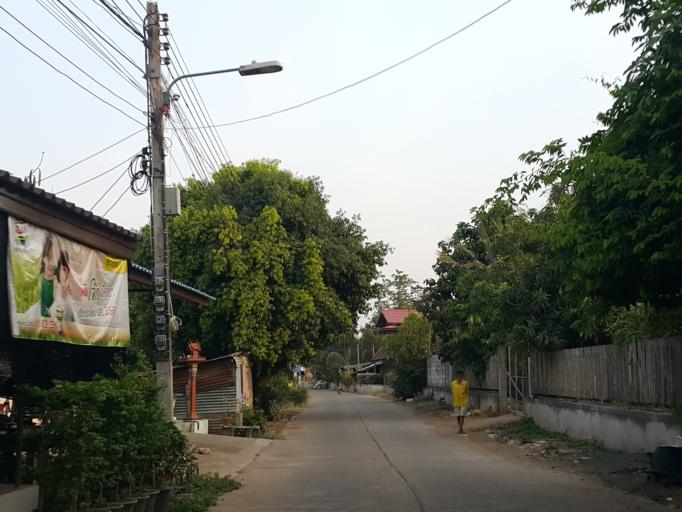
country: TH
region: Sukhothai
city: Sawankhalok
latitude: 17.2997
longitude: 99.8308
